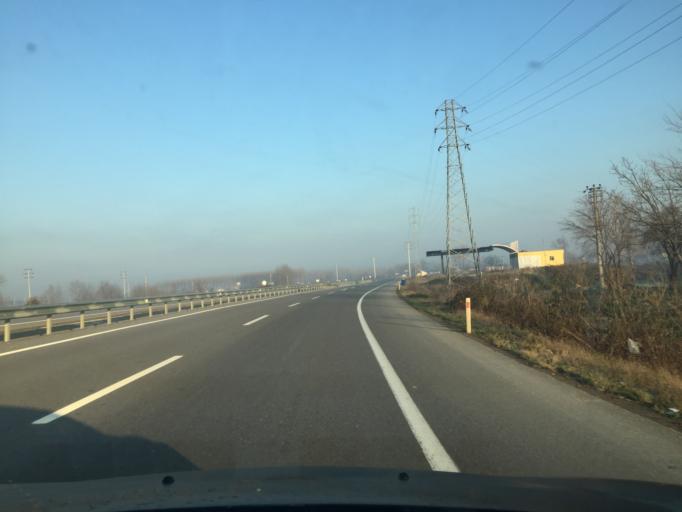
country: TR
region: Sakarya
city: Akyazi
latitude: 40.6420
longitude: 30.6136
